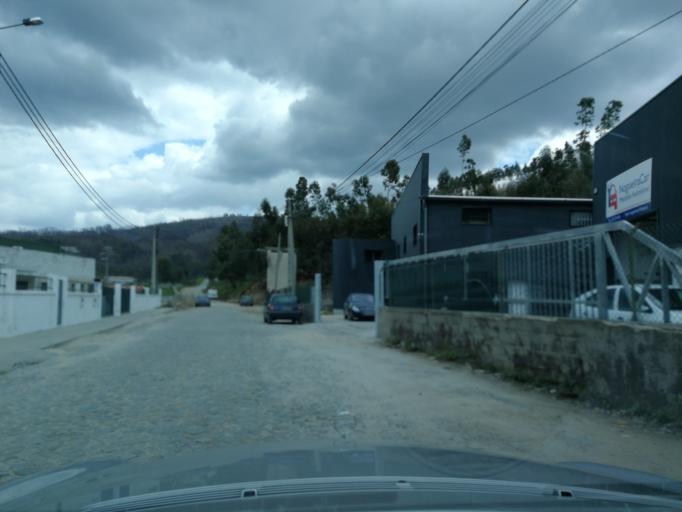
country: PT
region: Braga
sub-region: Braga
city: Braga
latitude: 41.5232
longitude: -8.3994
